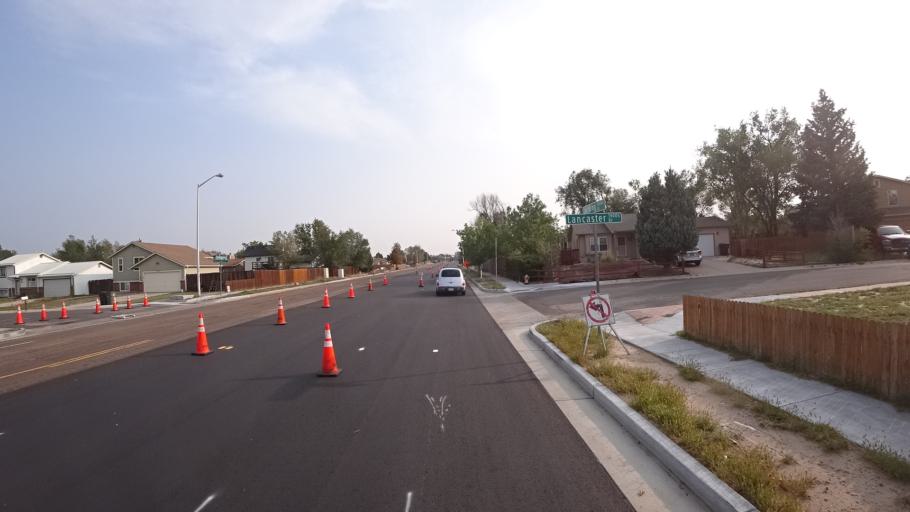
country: US
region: Colorado
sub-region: El Paso County
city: Stratmoor
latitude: 38.8058
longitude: -104.7441
